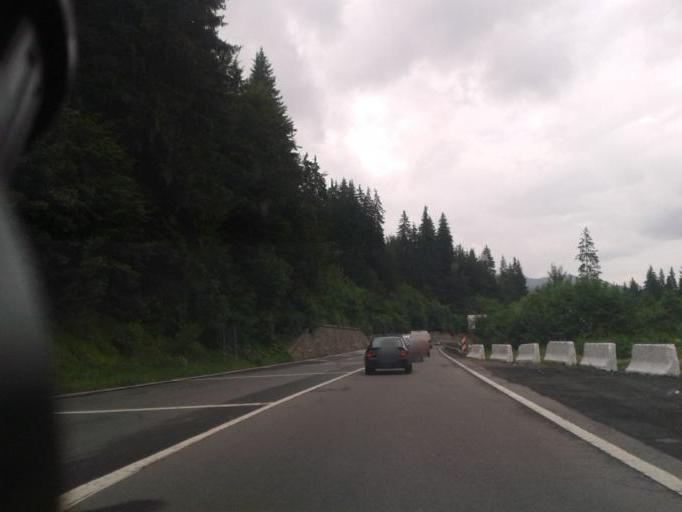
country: RO
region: Brasov
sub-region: Oras Predeal
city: Predeal
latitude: 45.5193
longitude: 25.5730
